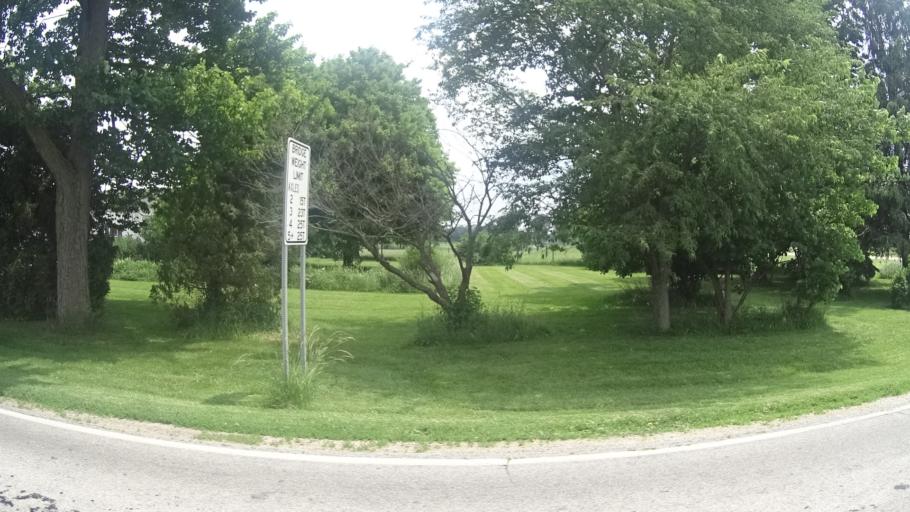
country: US
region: Ohio
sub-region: Erie County
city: Milan
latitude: 41.3230
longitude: -82.6314
